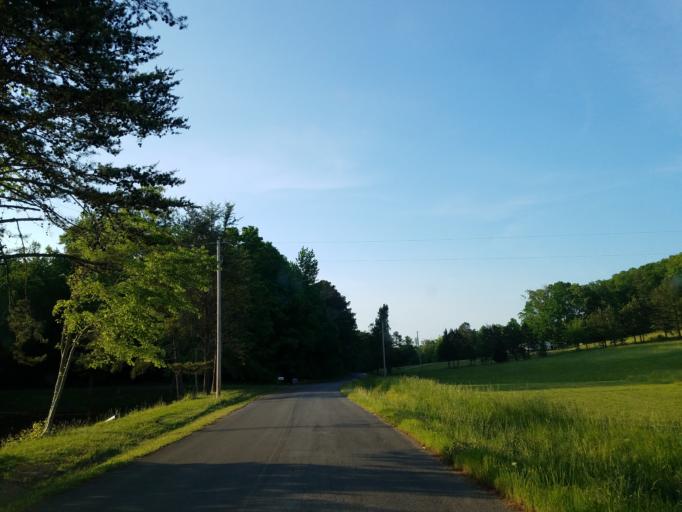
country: US
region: Georgia
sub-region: Whitfield County
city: Dalton
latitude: 34.6621
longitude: -85.0799
